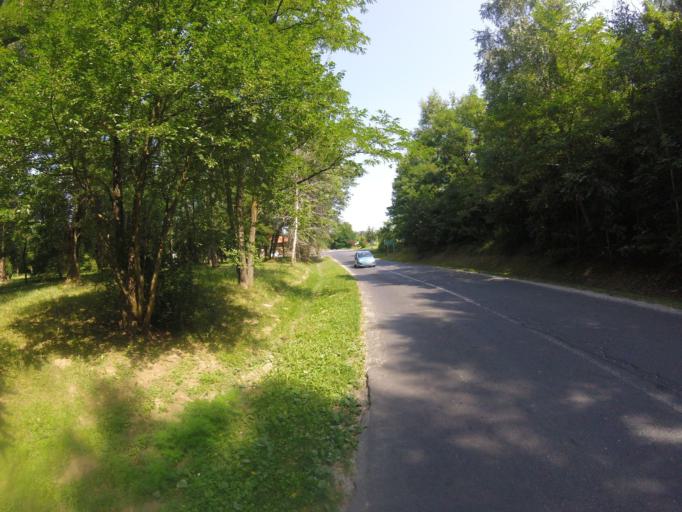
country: HU
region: Veszprem
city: Tapolca
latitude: 46.8073
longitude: 17.4349
